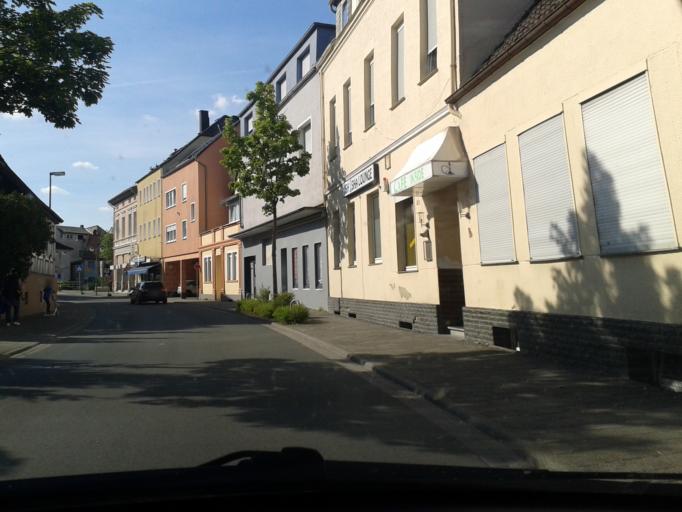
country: DE
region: North Rhine-Westphalia
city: Bad Lippspringe
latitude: 51.7815
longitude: 8.8212
